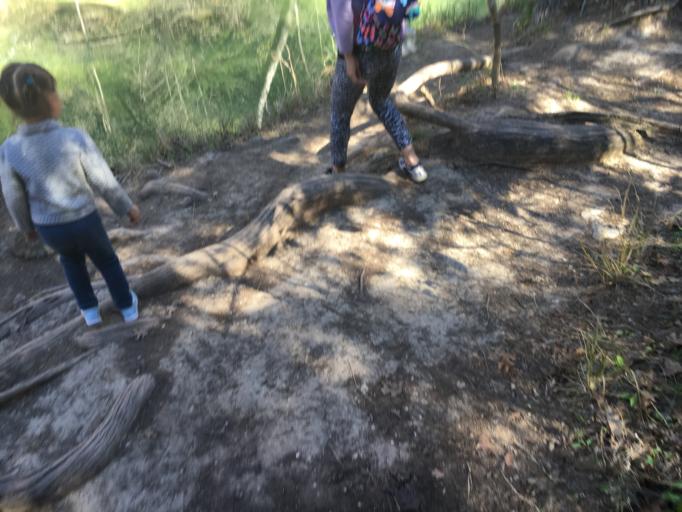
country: US
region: Texas
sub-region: Travis County
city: Briarcliff
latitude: 30.3444
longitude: -98.1302
